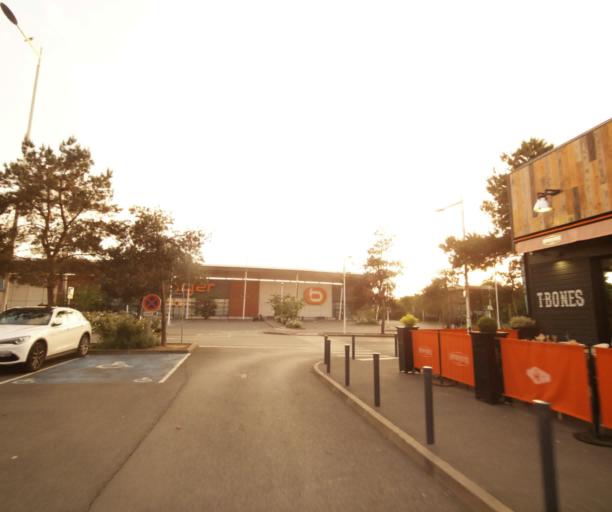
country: FR
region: Ile-de-France
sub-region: Departement des Hauts-de-Seine
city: Villeneuve-la-Garenne
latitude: 48.9338
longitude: 2.3181
